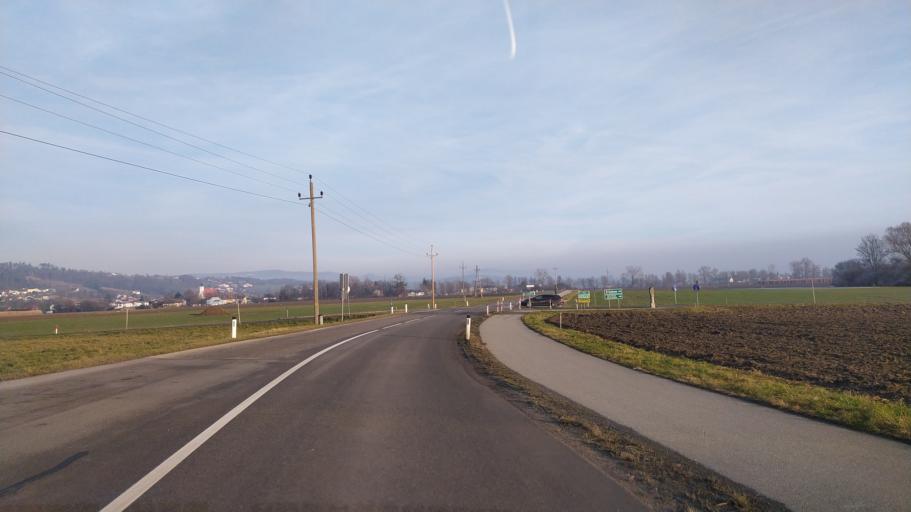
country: AT
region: Upper Austria
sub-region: Politischer Bezirk Urfahr-Umgebung
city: Feldkirchen an der Donau
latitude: 48.3473
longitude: 14.0609
